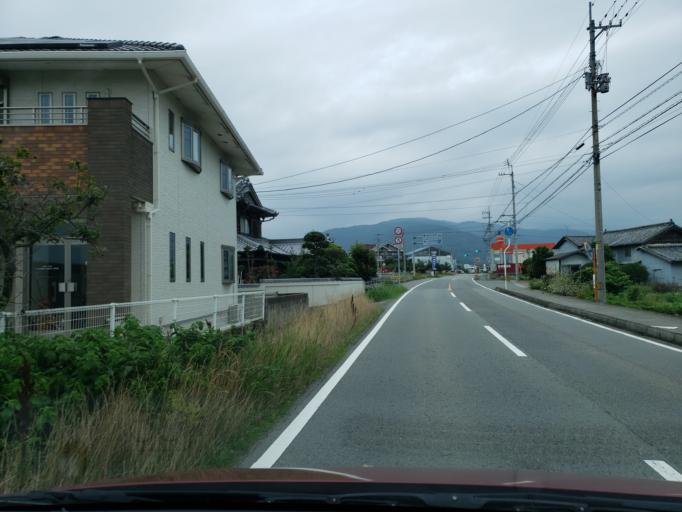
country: JP
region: Tokushima
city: Kamojimacho-jogejima
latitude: 34.1112
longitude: 134.3492
